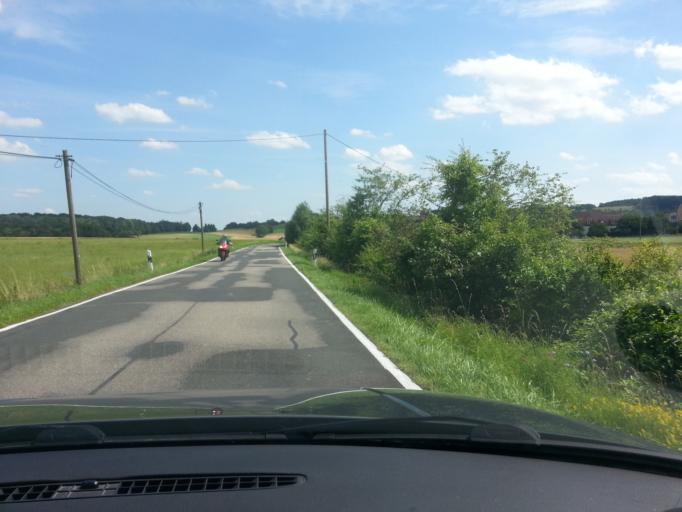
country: DE
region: Saarland
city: Blieskastel
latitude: 49.2015
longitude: 7.2812
